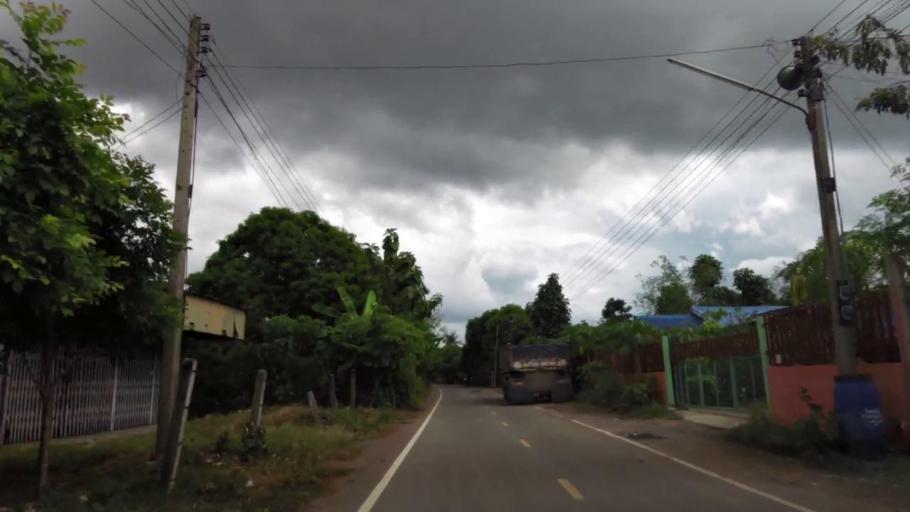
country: TH
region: Nakhon Sawan
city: Phai Sali
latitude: 15.6055
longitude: 100.6568
